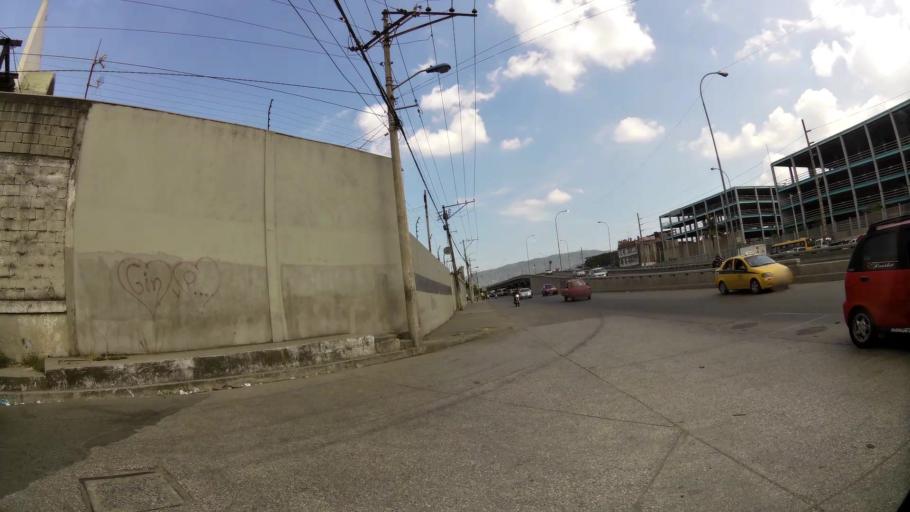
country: EC
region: Guayas
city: Guayaquil
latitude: -2.1279
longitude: -79.9321
